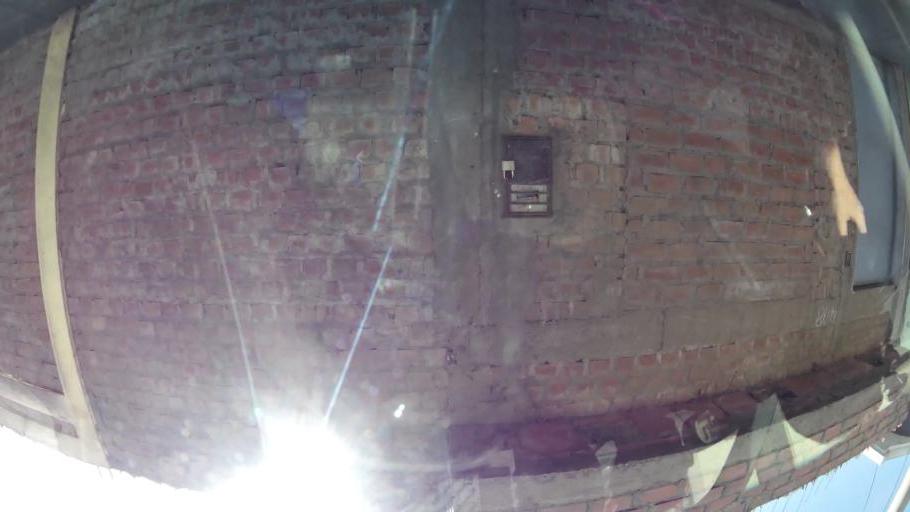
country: PE
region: Ica
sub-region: Provincia de Chincha
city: Chincha Alta
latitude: -13.4203
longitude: -76.1317
